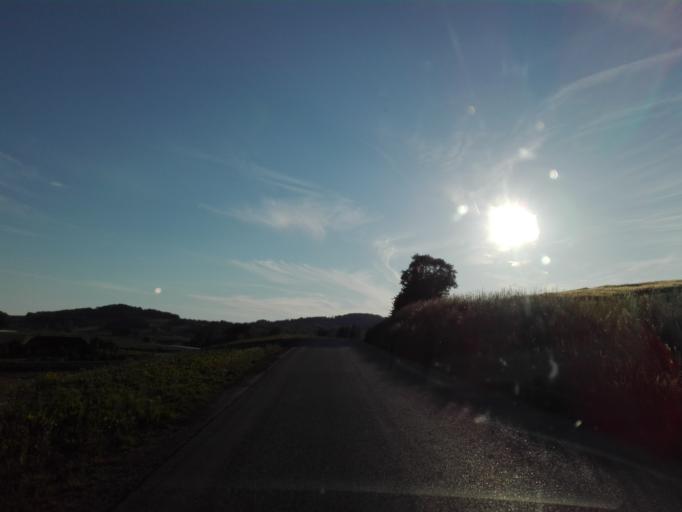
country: AT
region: Upper Austria
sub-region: Politischer Bezirk Urfahr-Umgebung
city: Feldkirchen an der Donau
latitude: 48.3095
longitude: 13.9960
